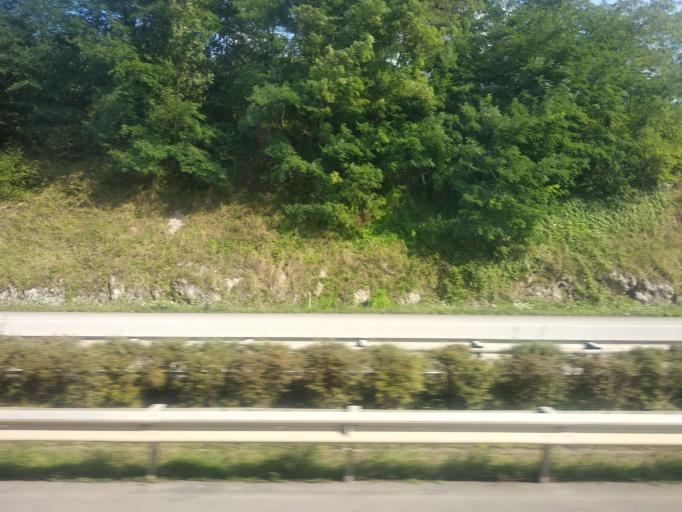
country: TR
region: Ordu
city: Ordu
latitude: 41.0104
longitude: 37.8322
